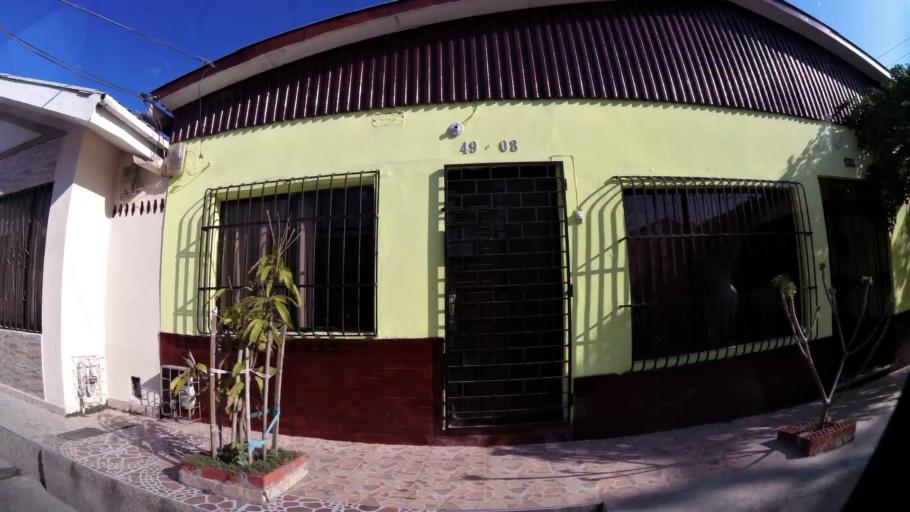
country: CO
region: Atlantico
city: Barranquilla
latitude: 10.9917
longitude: -74.7867
